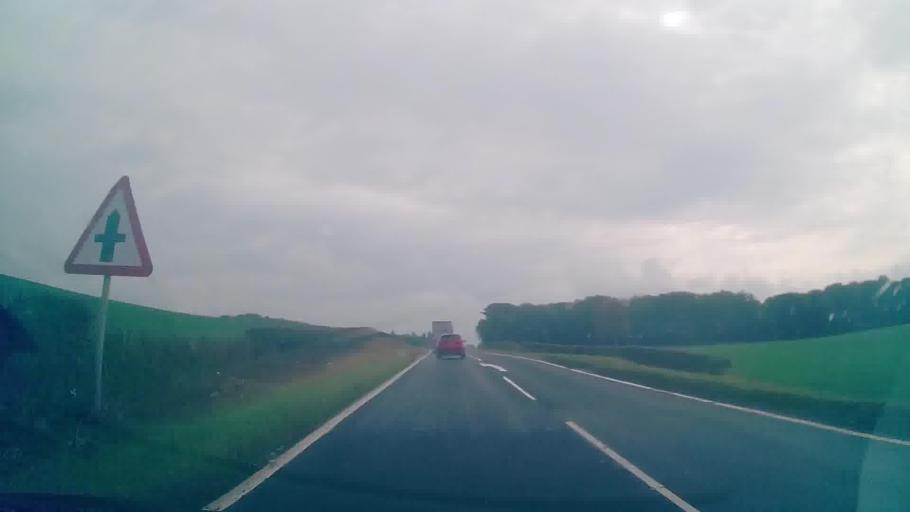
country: GB
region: Scotland
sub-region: Dumfries and Galloway
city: Lochmaben
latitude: 55.0418
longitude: -3.4427
